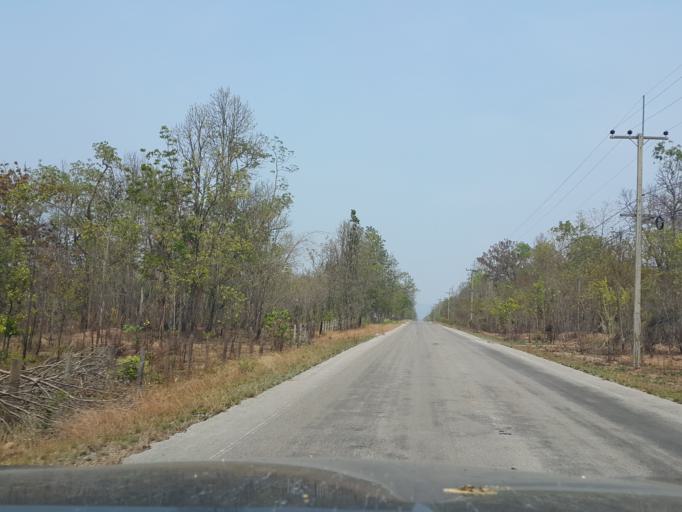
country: TH
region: Lampang
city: Mae Phrik
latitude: 17.5550
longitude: 99.1076
